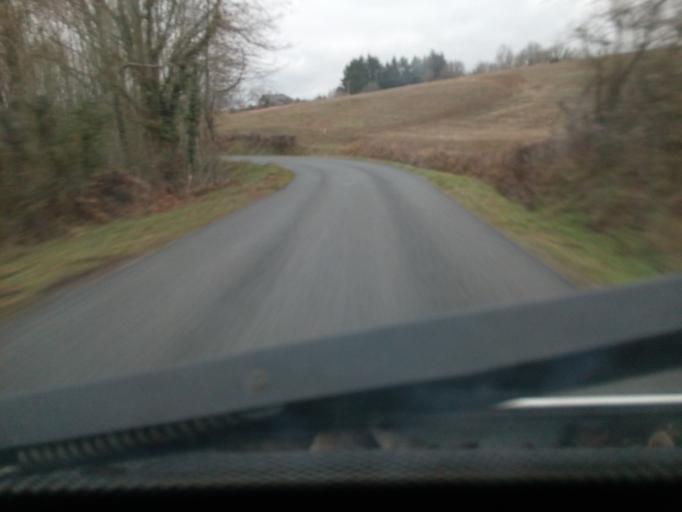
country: FR
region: Limousin
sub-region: Departement de la Creuse
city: Felletin
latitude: 45.8761
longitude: 2.1893
